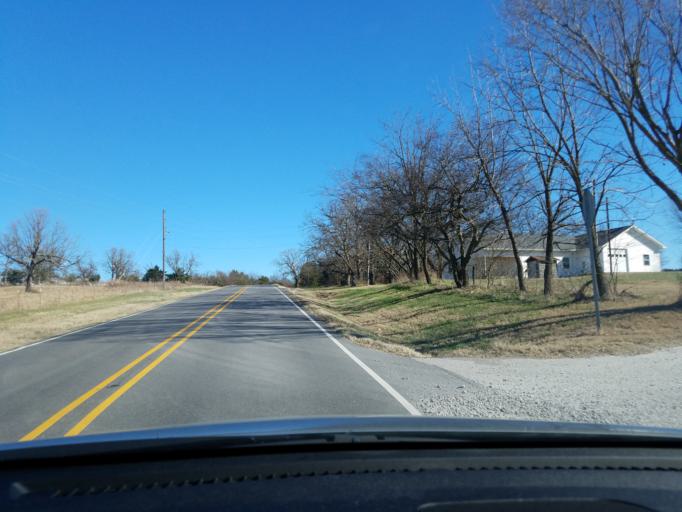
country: US
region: Arkansas
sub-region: Carroll County
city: Berryville
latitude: 36.4077
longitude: -93.5410
